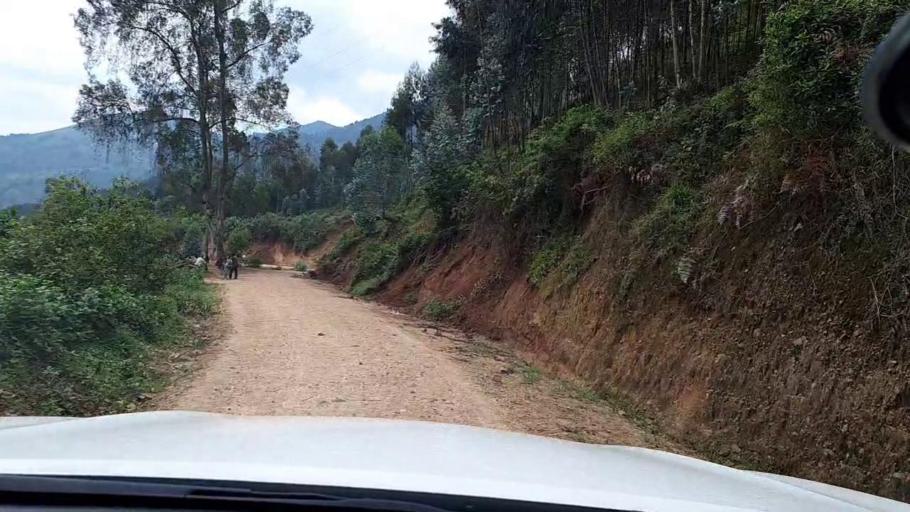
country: RW
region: Western Province
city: Kibuye
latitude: -2.2835
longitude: 29.3035
